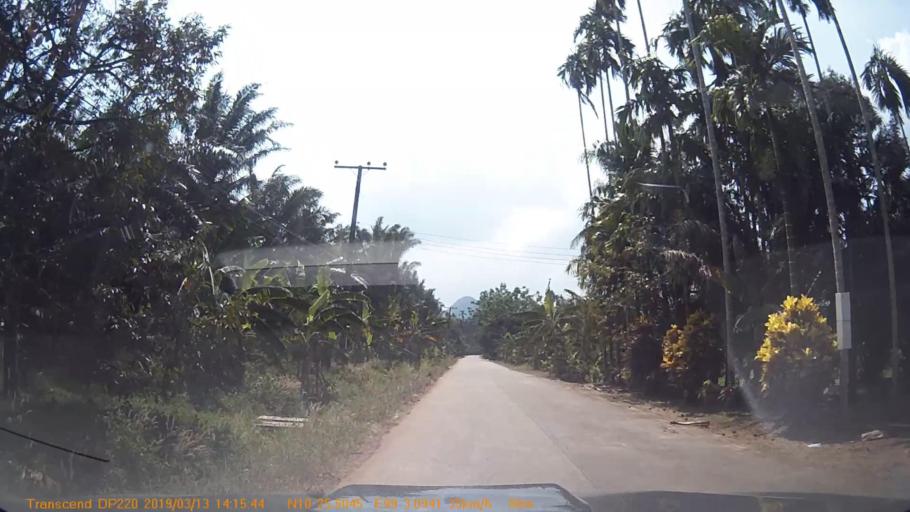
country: TH
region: Chumphon
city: Chumphon
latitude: 10.4253
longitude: 99.0526
